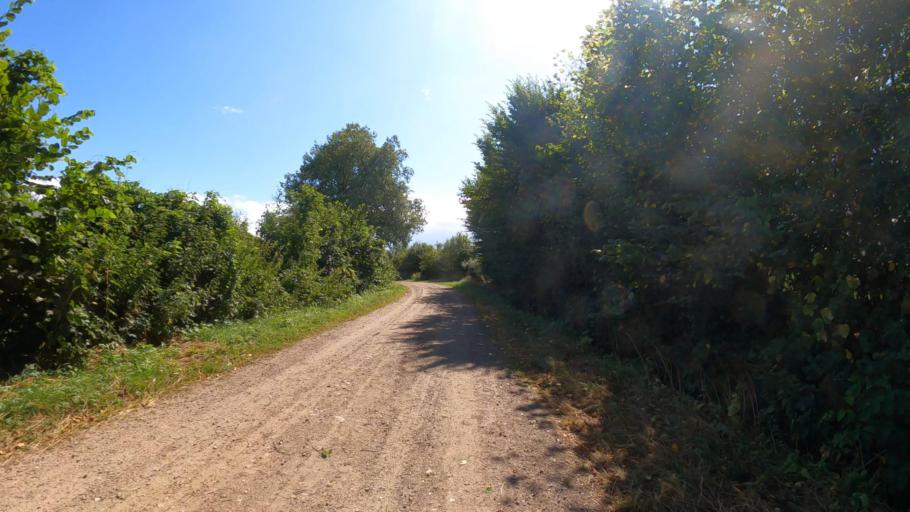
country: DE
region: Schleswig-Holstein
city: Wiemersdorf
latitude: 53.9544
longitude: 9.8967
